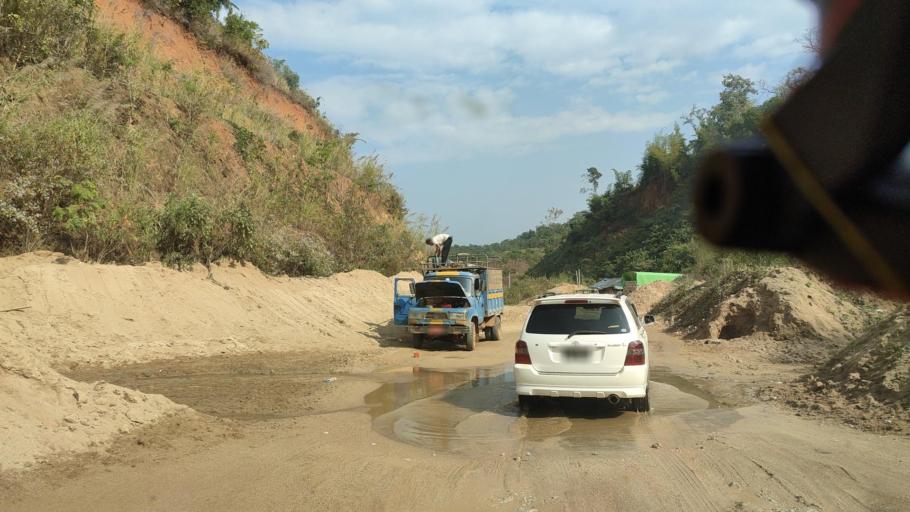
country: CN
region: Yunnan
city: Nayun
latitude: 21.7901
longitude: 99.5194
